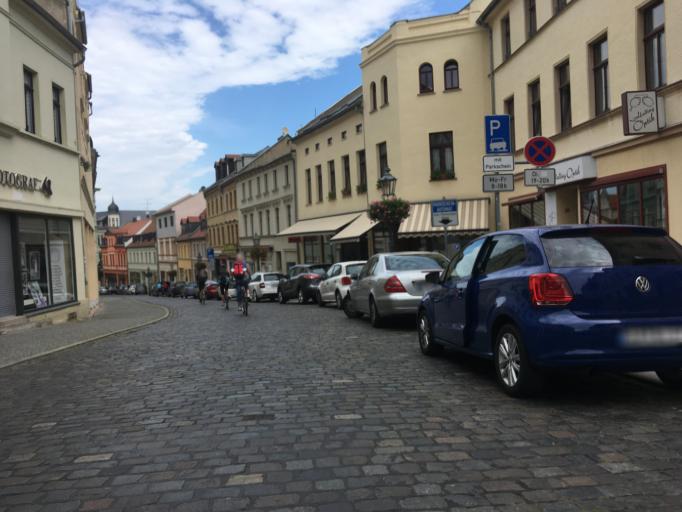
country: DE
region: Saxony-Anhalt
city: Bernburg
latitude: 51.7964
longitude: 11.7412
